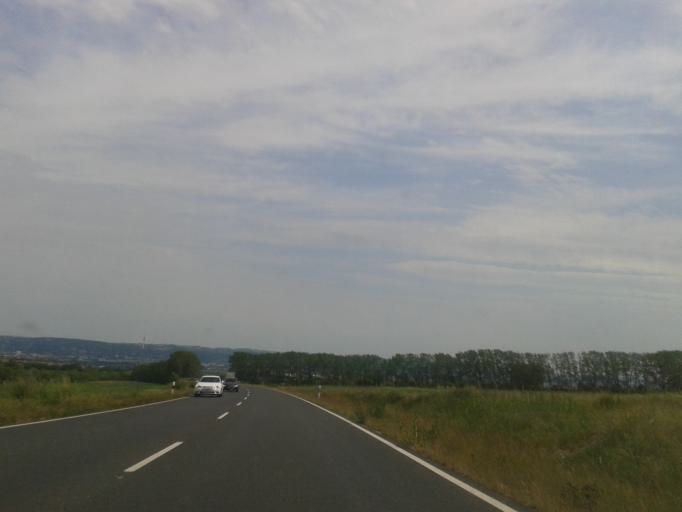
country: DE
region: Saxony
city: Bannewitz
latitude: 50.9886
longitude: 13.7443
